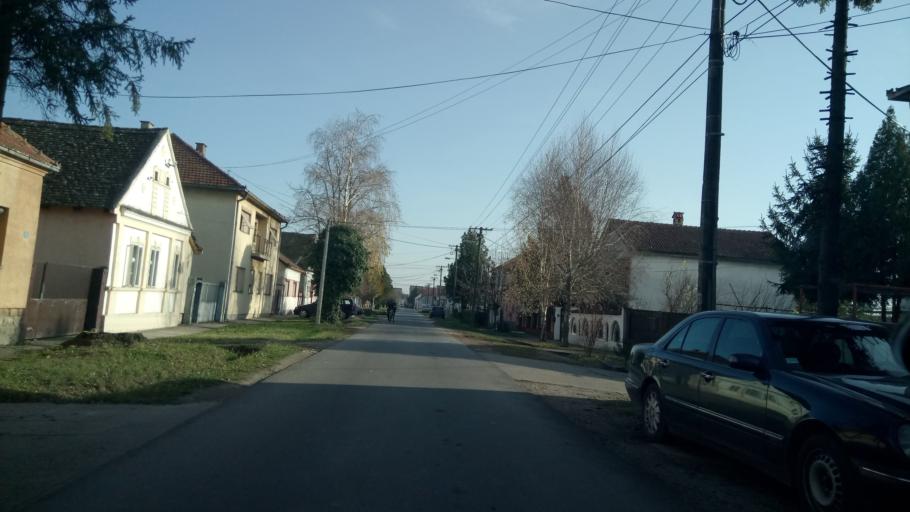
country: RS
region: Autonomna Pokrajina Vojvodina
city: Nova Pazova
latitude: 44.9494
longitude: 20.2180
